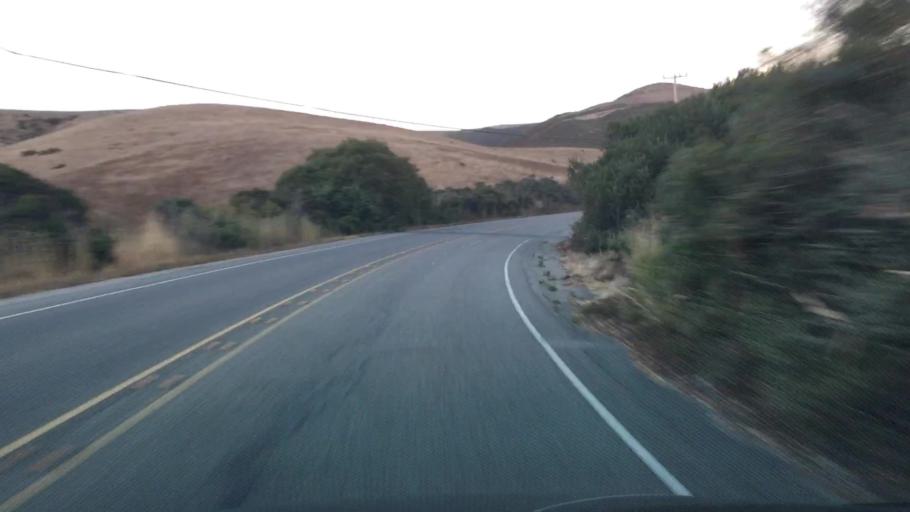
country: US
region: California
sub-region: San Mateo County
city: Half Moon Bay
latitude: 37.3304
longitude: -122.3827
